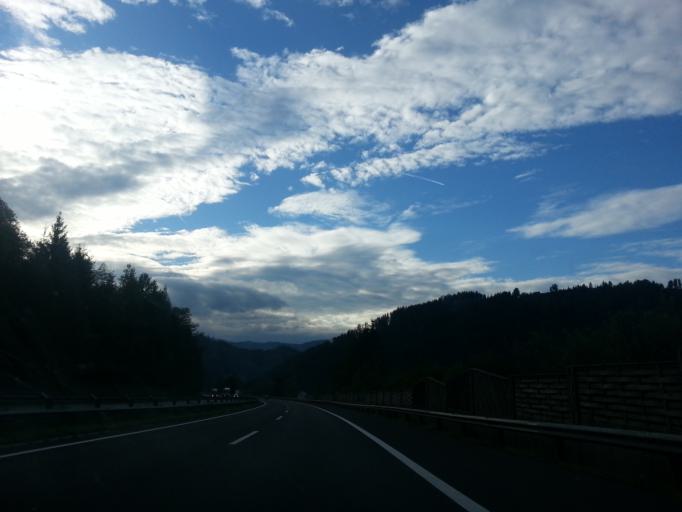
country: AT
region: Styria
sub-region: Politischer Bezirk Leoben
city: Sankt Michael in Obersteiermark
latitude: 47.3172
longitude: 15.0501
